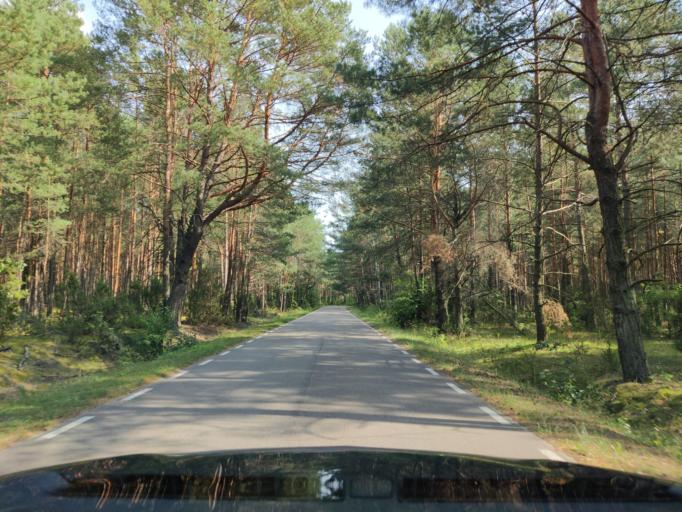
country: PL
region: Masovian Voivodeship
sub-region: Powiat wyszkowski
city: Dlugosiodlo
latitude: 52.8062
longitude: 21.4991
